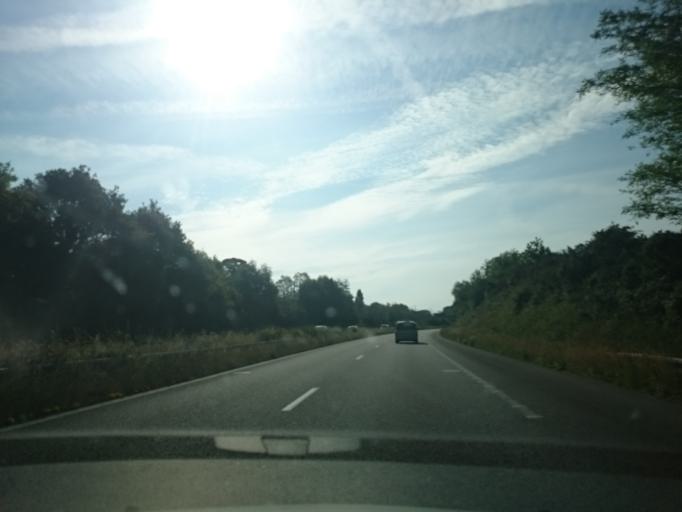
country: FR
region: Brittany
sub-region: Departement du Finistere
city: Quimperle
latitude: 47.8593
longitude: -3.5319
